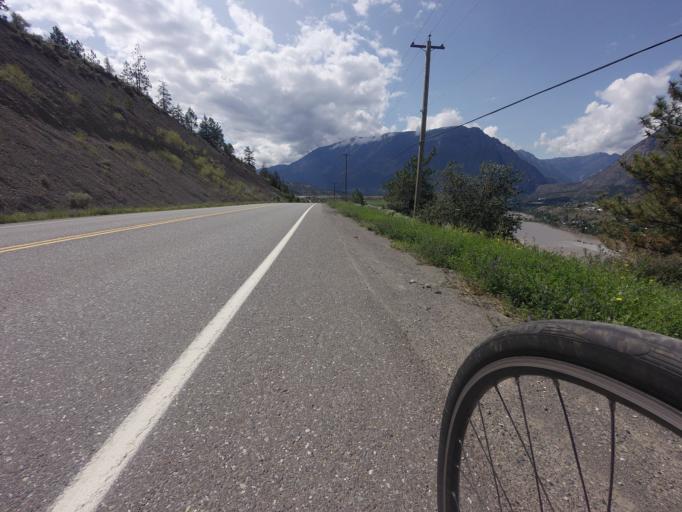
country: CA
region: British Columbia
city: Lillooet
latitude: 50.7102
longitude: -121.9085
